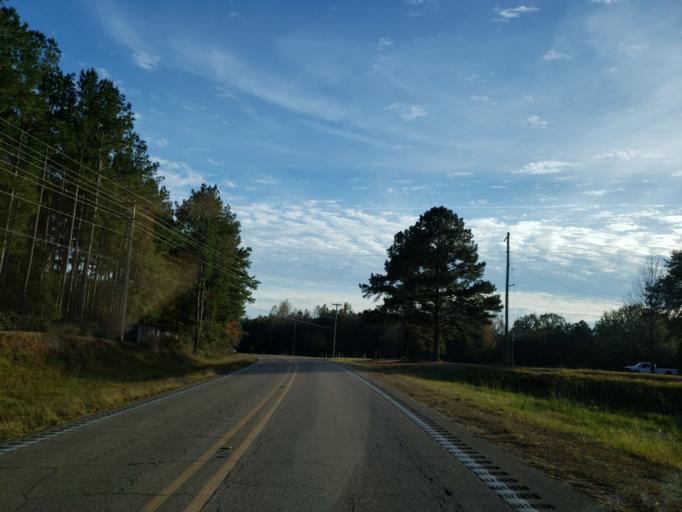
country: US
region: Mississippi
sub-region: Lamar County
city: West Hattiesburg
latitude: 31.2903
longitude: -89.4709
